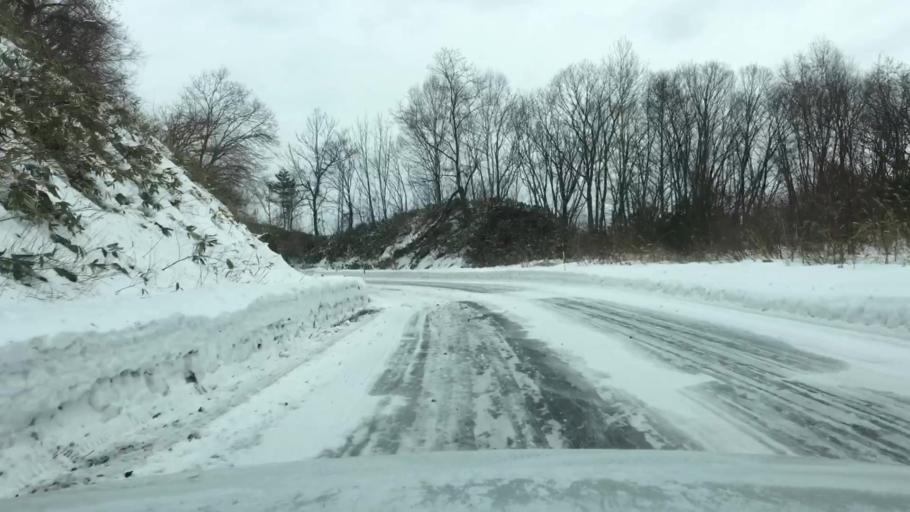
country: JP
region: Iwate
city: Shizukuishi
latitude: 39.9423
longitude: 140.9970
